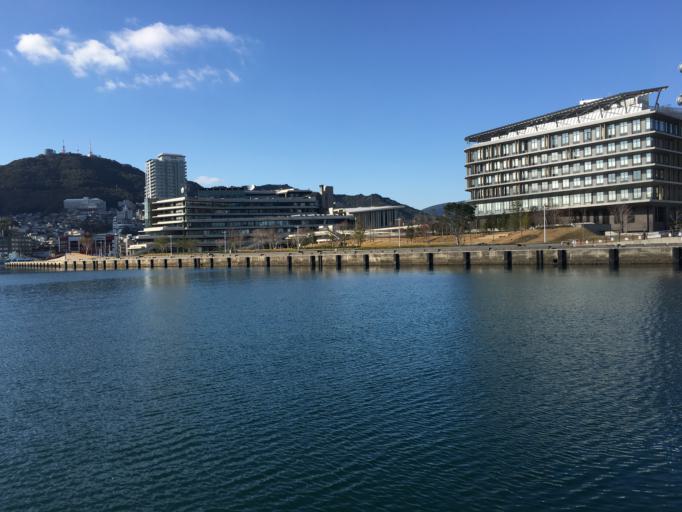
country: JP
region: Nagasaki
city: Nagasaki-shi
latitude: 32.7482
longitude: 129.8707
